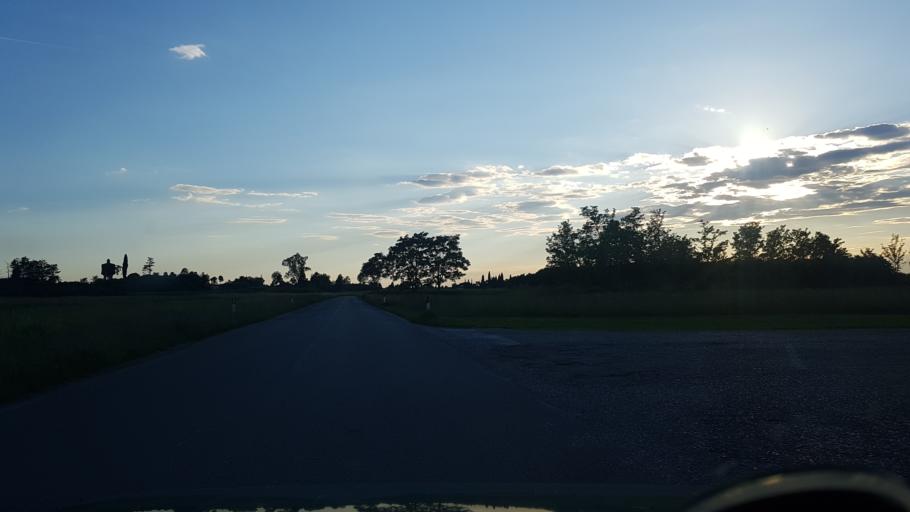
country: IT
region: Friuli Venezia Giulia
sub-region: Provincia di Udine
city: Sottoselva
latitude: 45.9113
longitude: 13.3176
